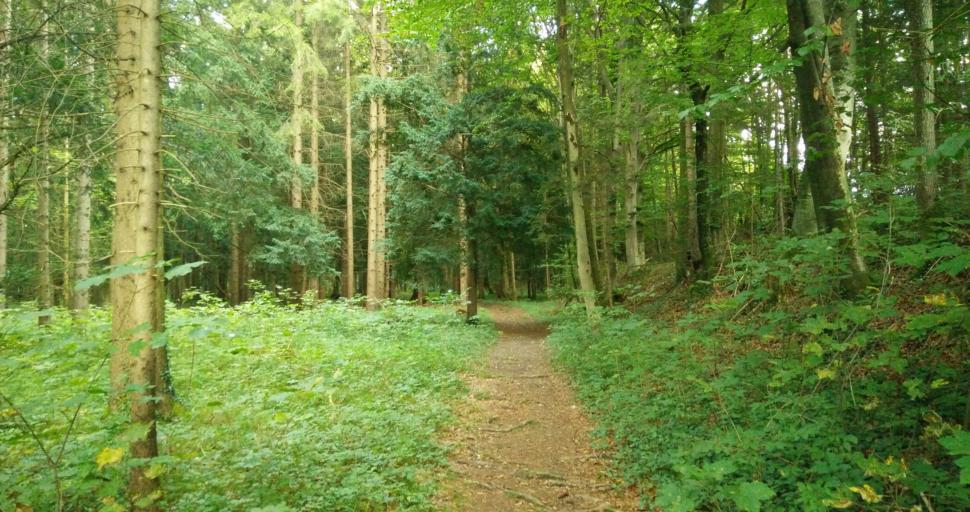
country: AT
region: Salzburg
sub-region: Politischer Bezirk Hallein
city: Adnet
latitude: 47.6571
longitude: 13.1415
